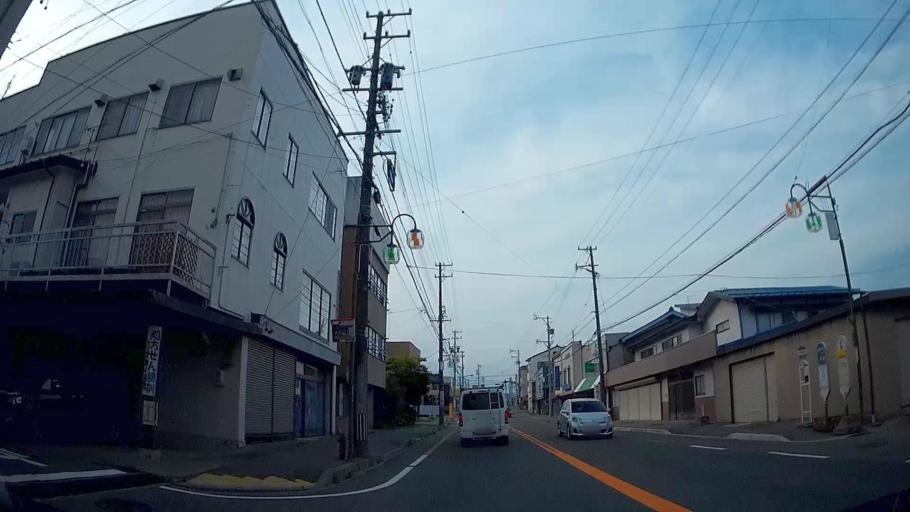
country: JP
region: Nagano
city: Ina
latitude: 35.8073
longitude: 137.9443
